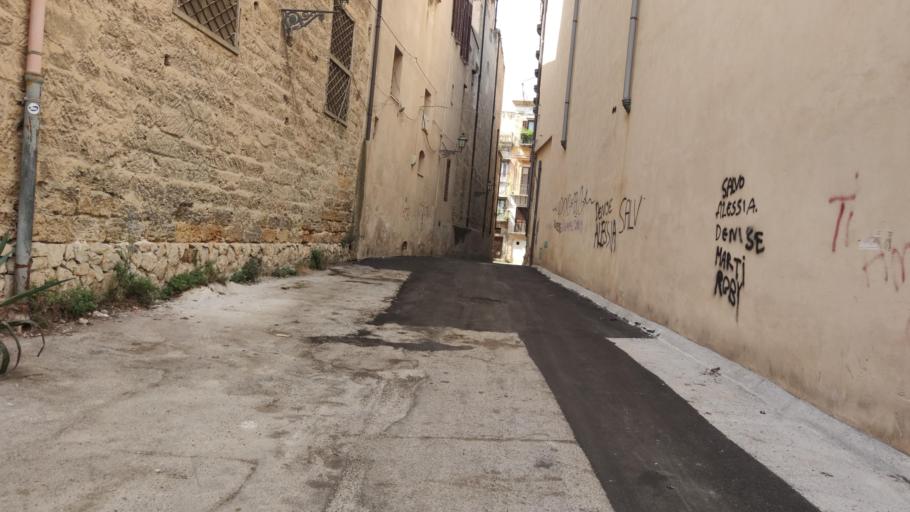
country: IT
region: Sicily
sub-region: Palermo
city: Palermo
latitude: 38.1162
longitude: 13.3712
